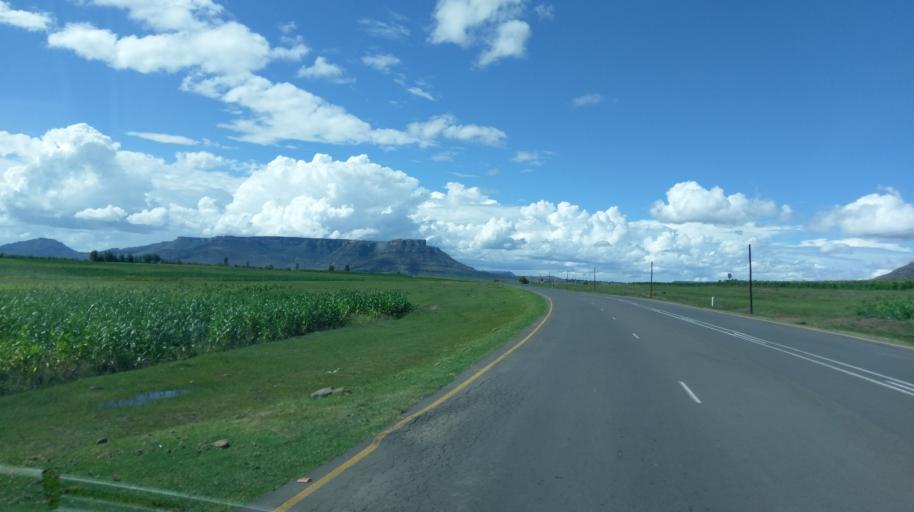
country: LS
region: Mafeteng
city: Mafeteng
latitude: -29.6839
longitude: 27.4442
